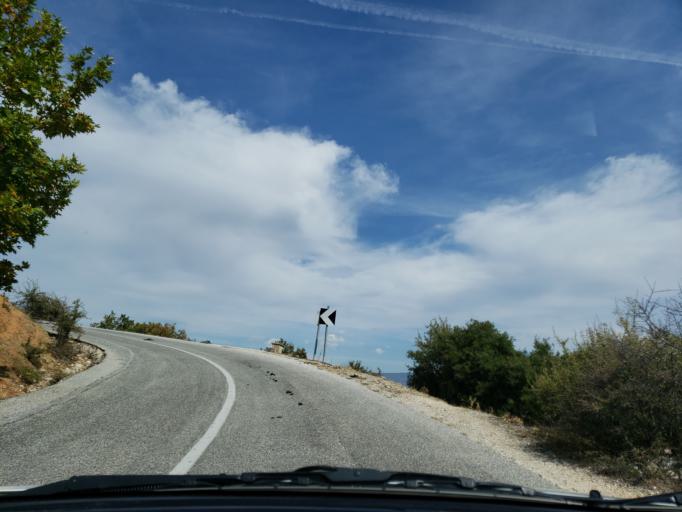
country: GR
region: Thessaly
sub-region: Trikala
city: Kalampaka
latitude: 39.7238
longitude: 21.6495
